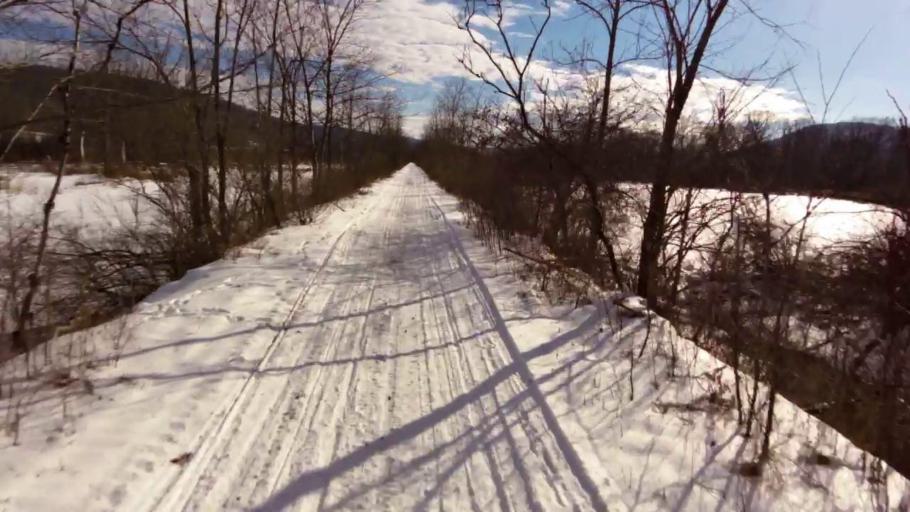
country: US
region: Pennsylvania
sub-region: McKean County
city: Foster Brook
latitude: 42.0074
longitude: -78.6241
